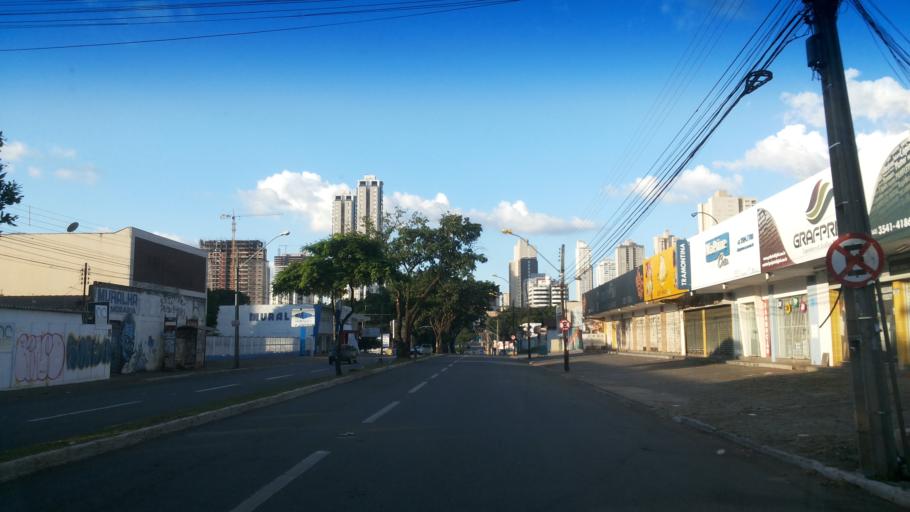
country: BR
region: Goias
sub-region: Goiania
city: Goiania
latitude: -16.7064
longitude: -49.2782
